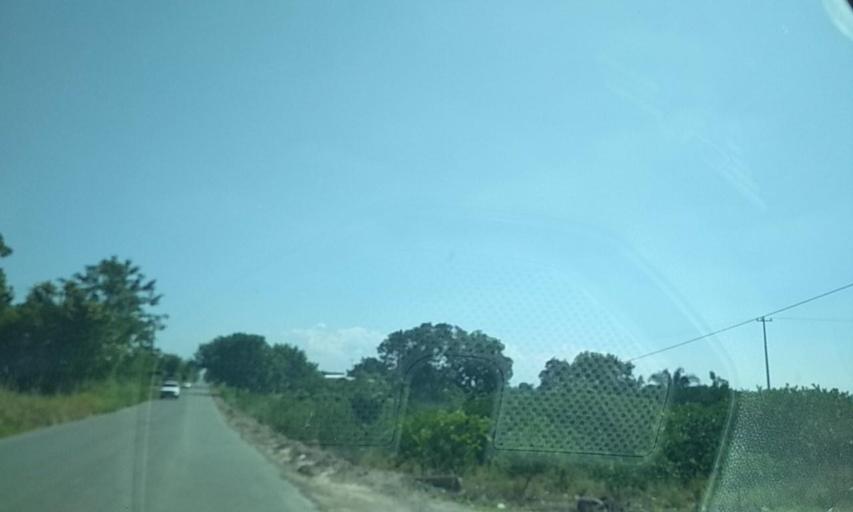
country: MX
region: Veracruz
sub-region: Martinez de la Torre
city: La Union Paso Largo
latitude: 20.1507
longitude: -97.0008
